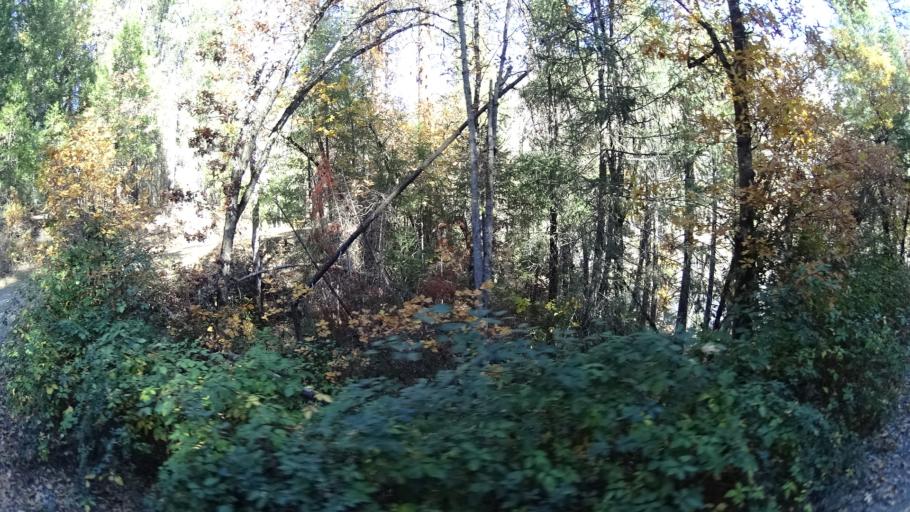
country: US
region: California
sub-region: Siskiyou County
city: Yreka
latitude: 41.8639
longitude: -122.7921
